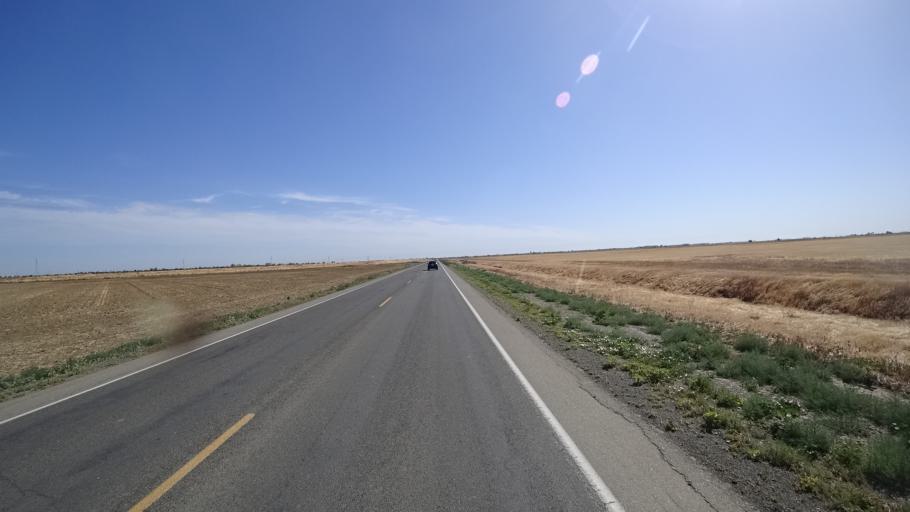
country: US
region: California
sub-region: Kings County
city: Lemoore Station
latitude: 36.2354
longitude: -119.8865
